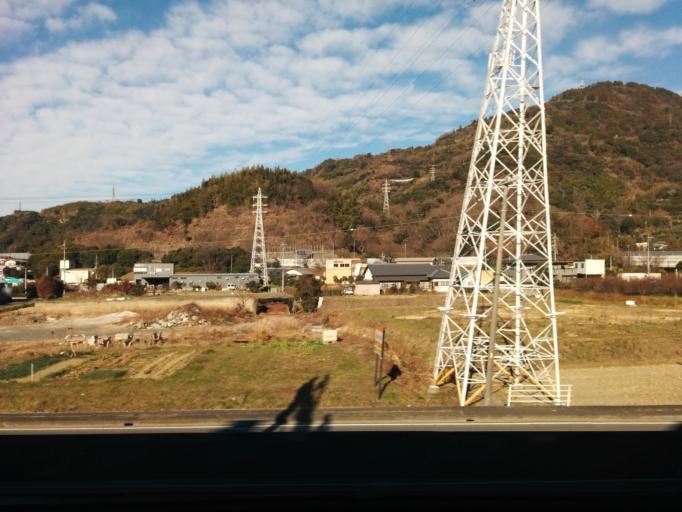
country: JP
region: Shizuoka
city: Yaizu
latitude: 34.8901
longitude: 138.3289
